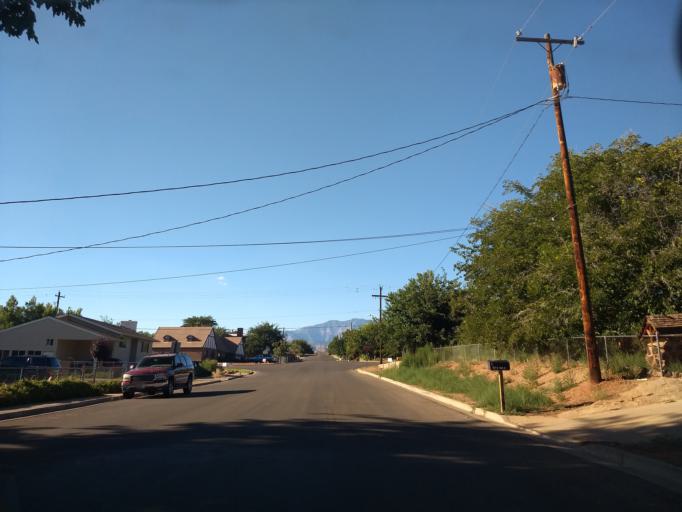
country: US
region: Utah
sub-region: Washington County
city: Washington
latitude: 37.1351
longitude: -113.5065
